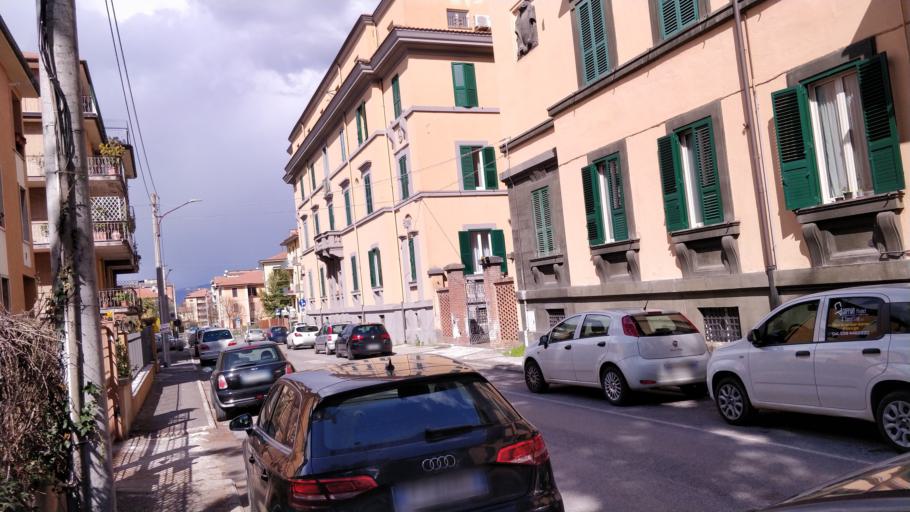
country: IT
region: Latium
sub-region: Provincia di Rieti
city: Rieti
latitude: 42.4047
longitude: 12.8548
